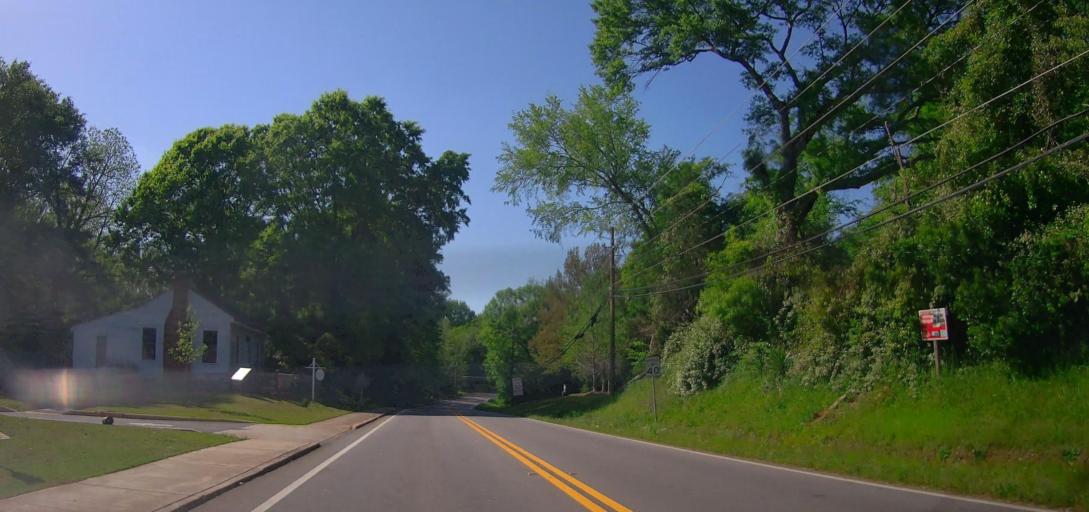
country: US
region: Georgia
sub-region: Morgan County
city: Madison
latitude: 33.5998
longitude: -83.4728
